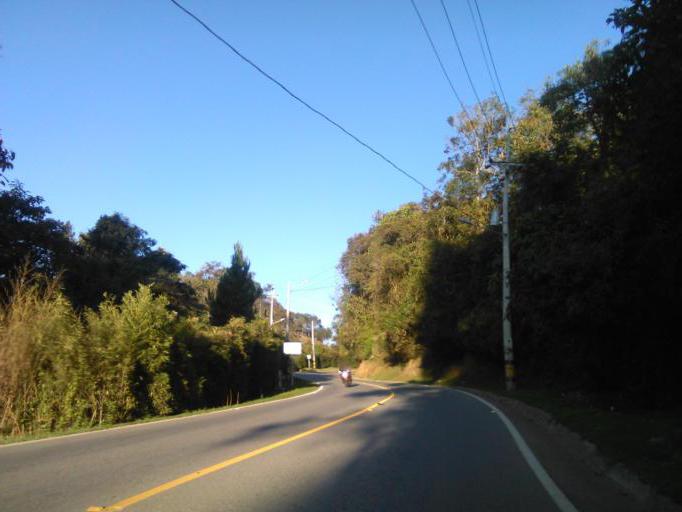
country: CO
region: Antioquia
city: La Union
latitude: 6.0023
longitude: -75.3840
